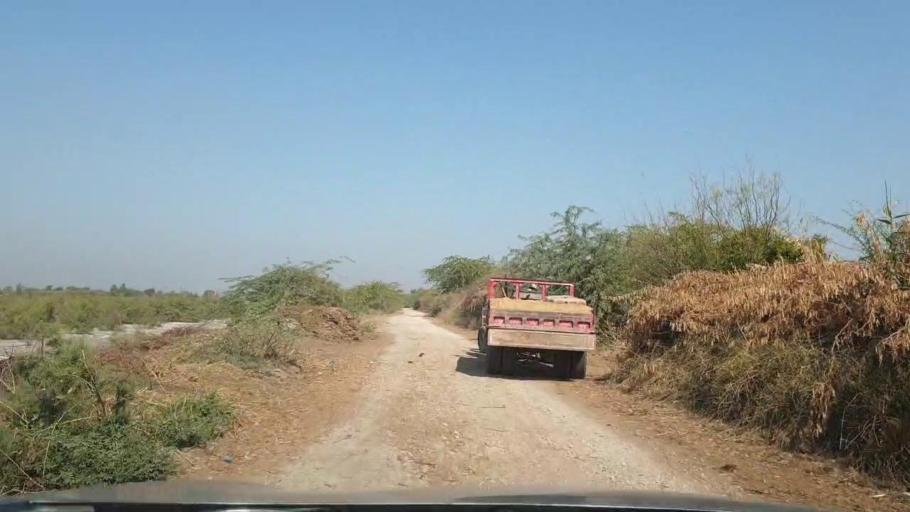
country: PK
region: Sindh
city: Berani
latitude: 25.6775
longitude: 68.8962
